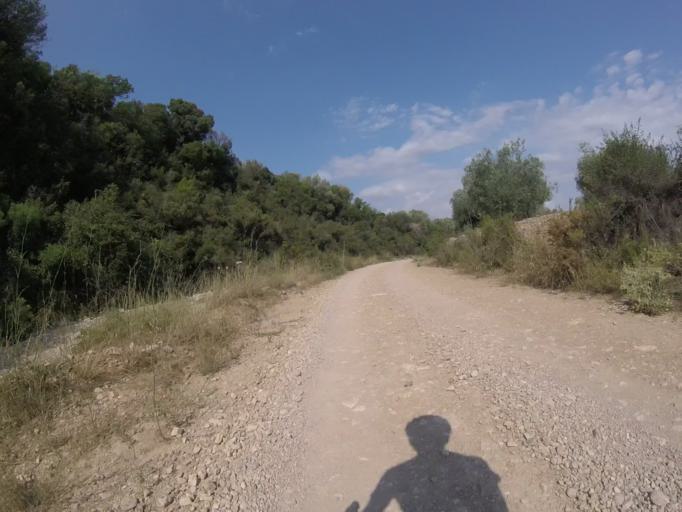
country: ES
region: Valencia
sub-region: Provincia de Castello
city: Cuevas de Vinroma
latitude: 40.3083
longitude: 0.1751
